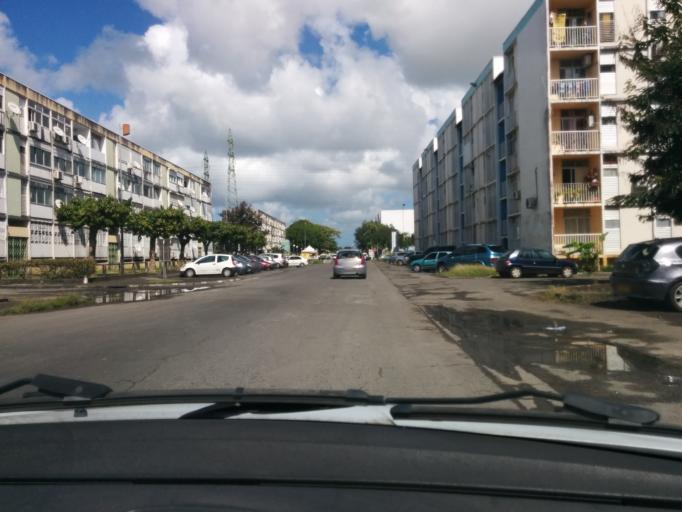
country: GP
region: Guadeloupe
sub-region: Guadeloupe
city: Pointe-a-Pitre
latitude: 16.2532
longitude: -61.5305
